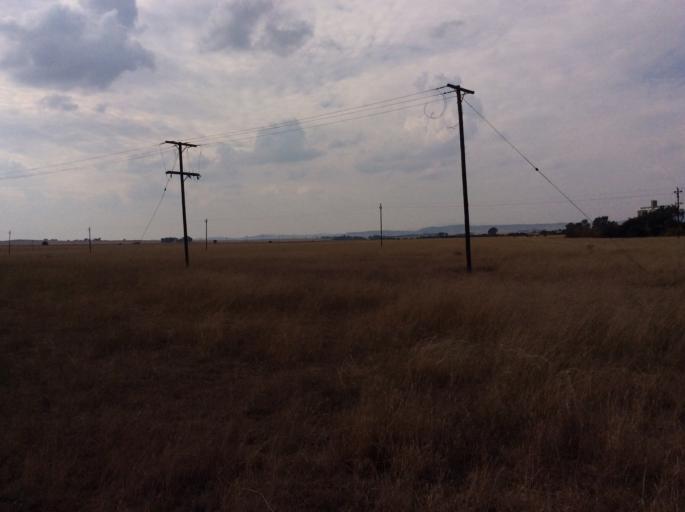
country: ZA
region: Orange Free State
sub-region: Xhariep District Municipality
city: Dewetsdorp
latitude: -29.5758
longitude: 26.6745
